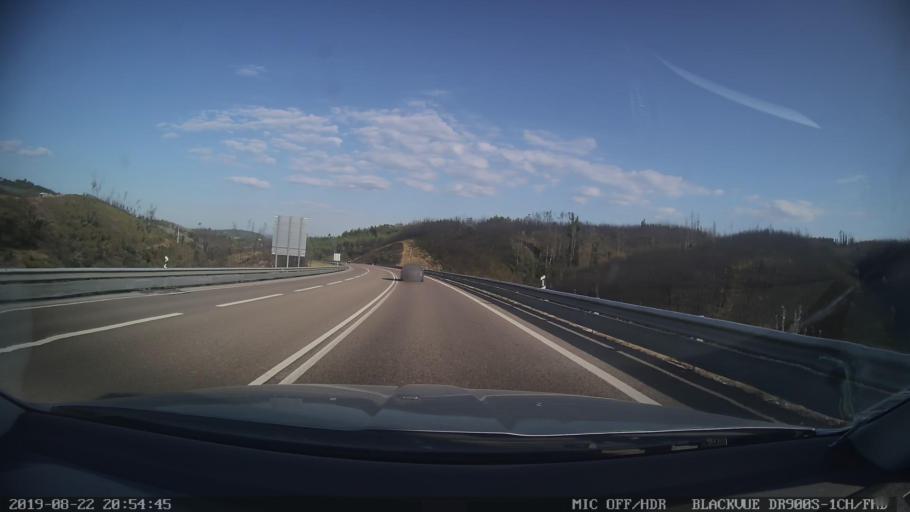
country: PT
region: Castelo Branco
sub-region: Serta
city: Serta
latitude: 39.7764
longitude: -8.0185
